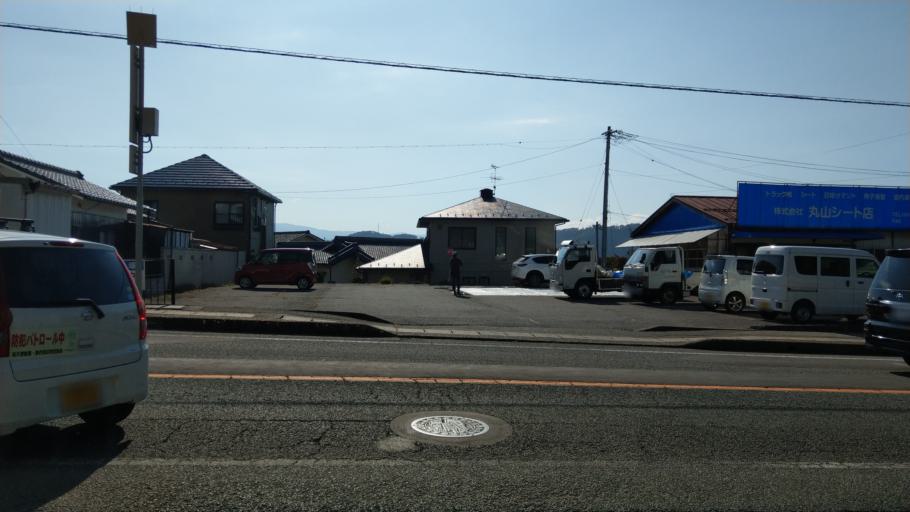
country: JP
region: Nagano
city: Komoro
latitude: 36.3161
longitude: 138.4370
